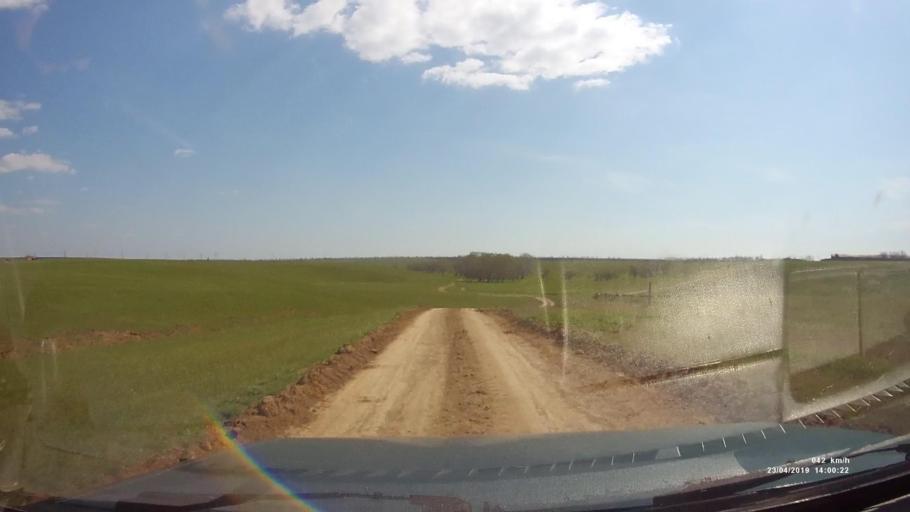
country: RU
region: Rostov
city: Remontnoye
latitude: 46.5600
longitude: 42.9468
